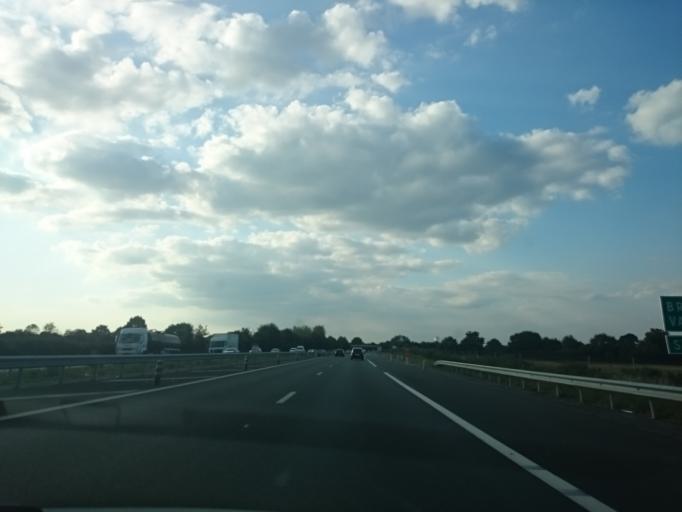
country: FR
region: Pays de la Loire
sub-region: Departement de la Loire-Atlantique
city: Sautron
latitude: 47.2657
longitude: -1.7086
